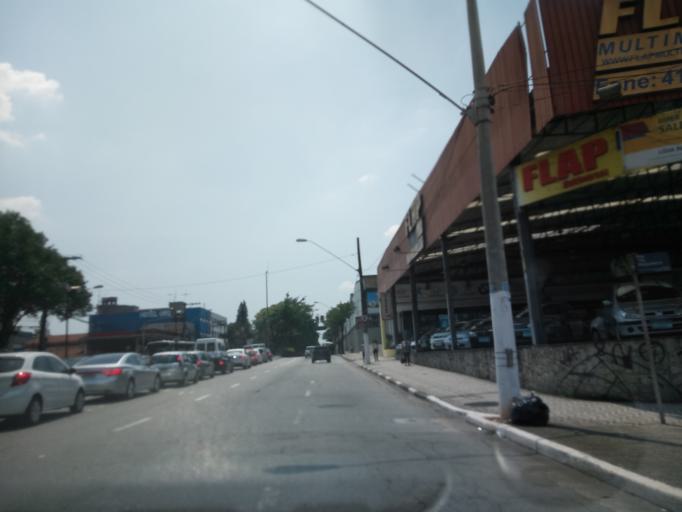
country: BR
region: Sao Paulo
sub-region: Sao Bernardo Do Campo
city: Sao Bernardo do Campo
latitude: -23.6655
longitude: -46.5689
